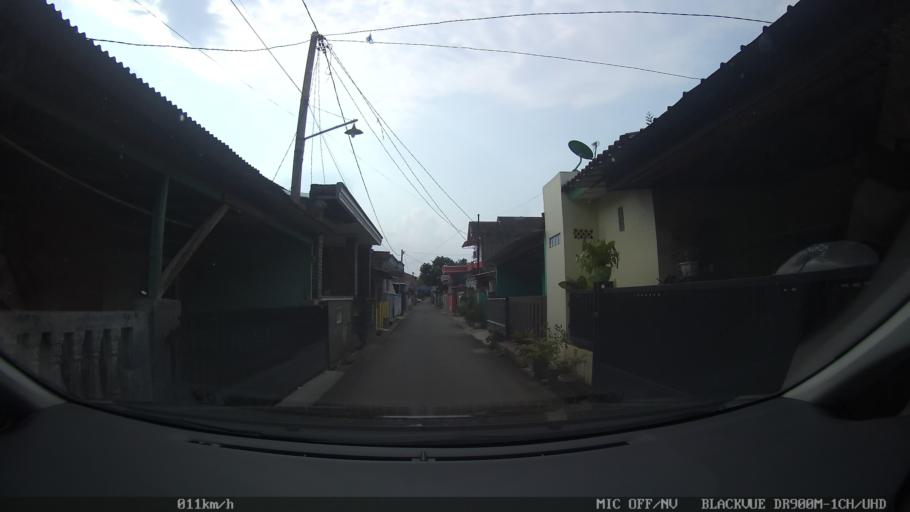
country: ID
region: Lampung
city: Kedaton
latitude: -5.3706
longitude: 105.2176
